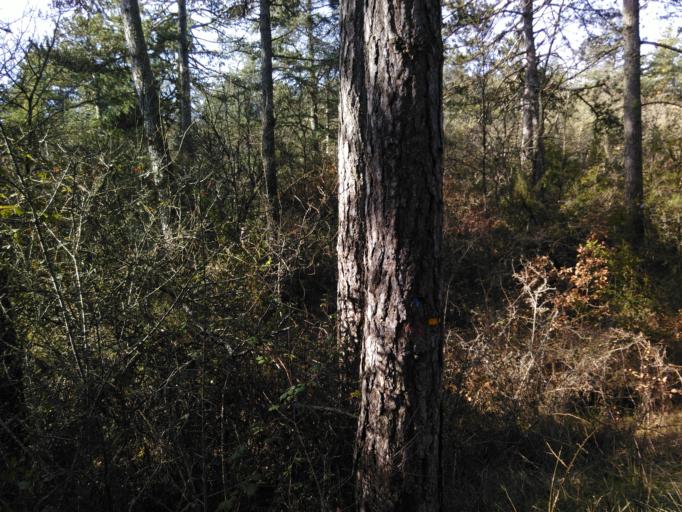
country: FR
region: Provence-Alpes-Cote d'Azur
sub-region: Departement du Vaucluse
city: Venasque
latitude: 43.9628
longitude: 5.1725
